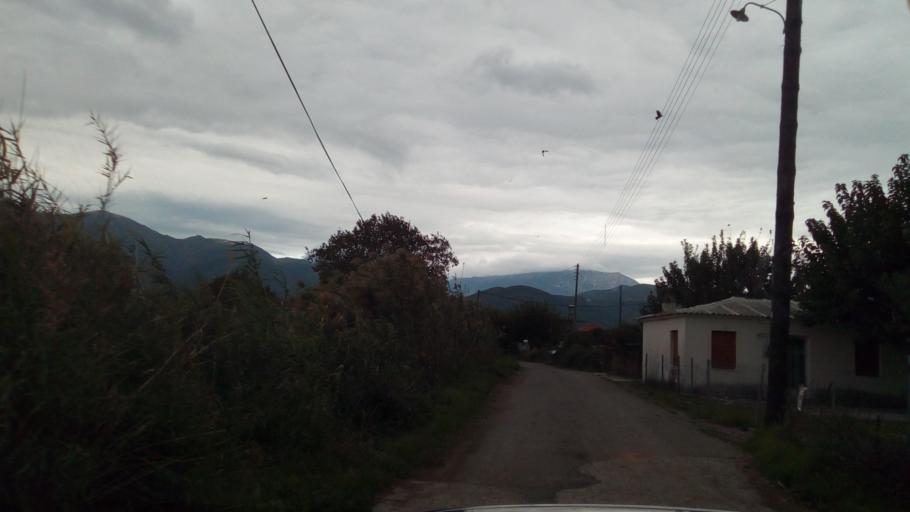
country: GR
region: West Greece
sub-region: Nomos Aitolias kai Akarnanias
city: Nafpaktos
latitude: 38.3928
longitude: 21.8871
